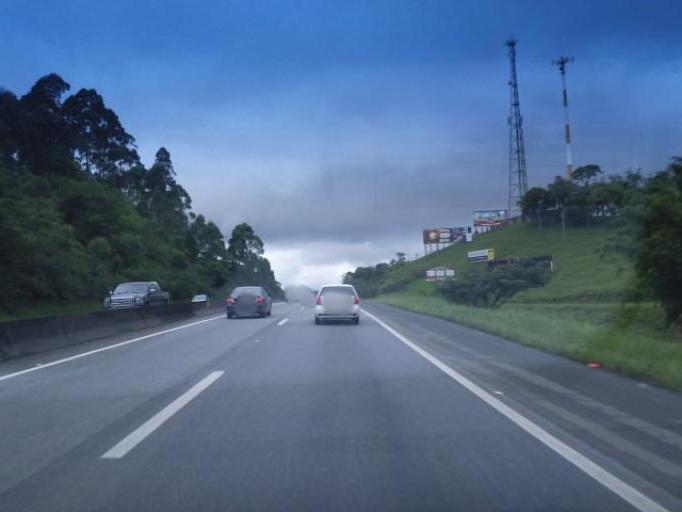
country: BR
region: Santa Catarina
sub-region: Balneario Camboriu
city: Balneario Camboriu
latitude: -26.9710
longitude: -48.6832
